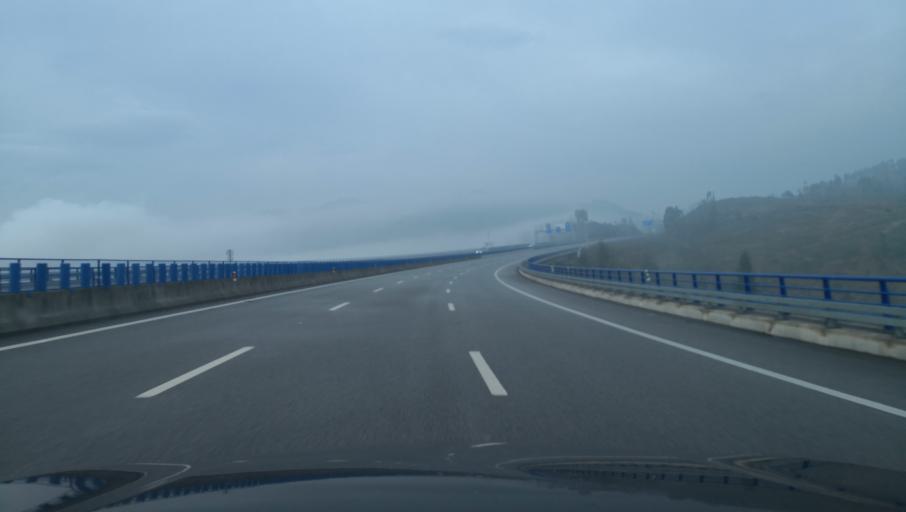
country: PT
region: Porto
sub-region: Paredes
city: Recarei
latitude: 41.1358
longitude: -8.4258
